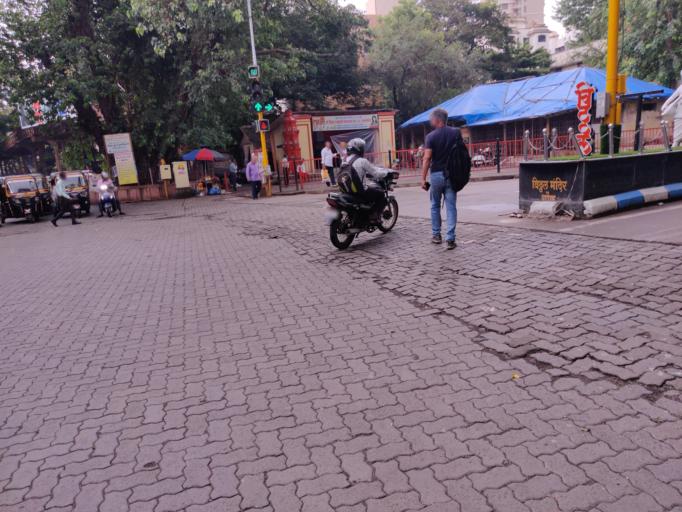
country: IN
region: Maharashtra
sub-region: Mumbai Suburban
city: Borivli
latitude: 19.2549
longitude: 72.8579
